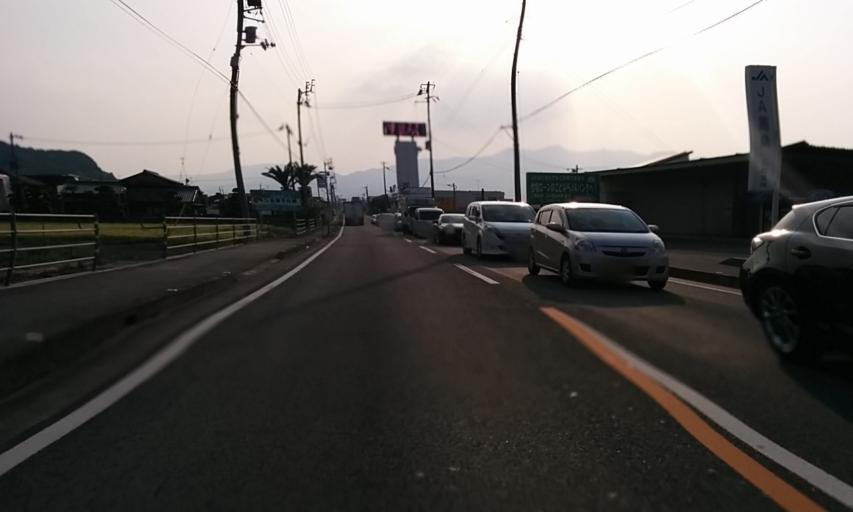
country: JP
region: Ehime
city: Saijo
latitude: 33.8970
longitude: 133.1073
